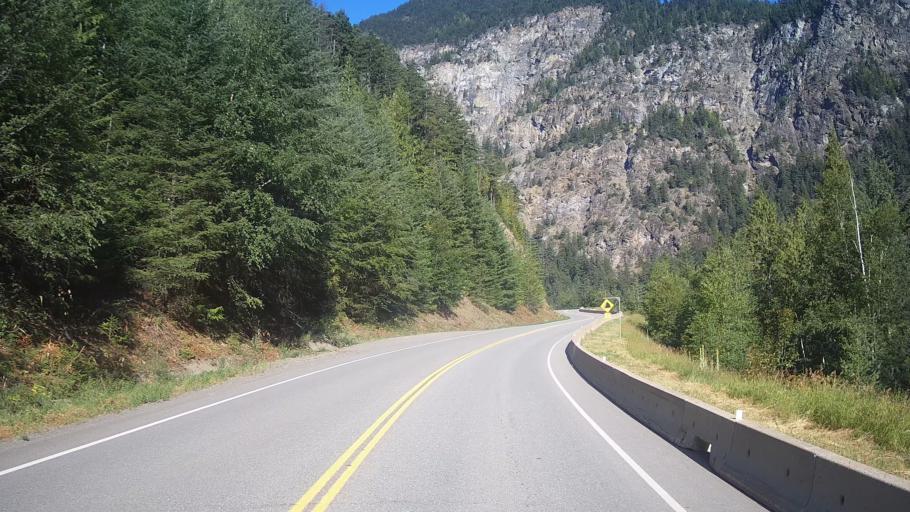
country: CA
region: British Columbia
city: Lillooet
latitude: 50.6452
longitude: -122.0649
